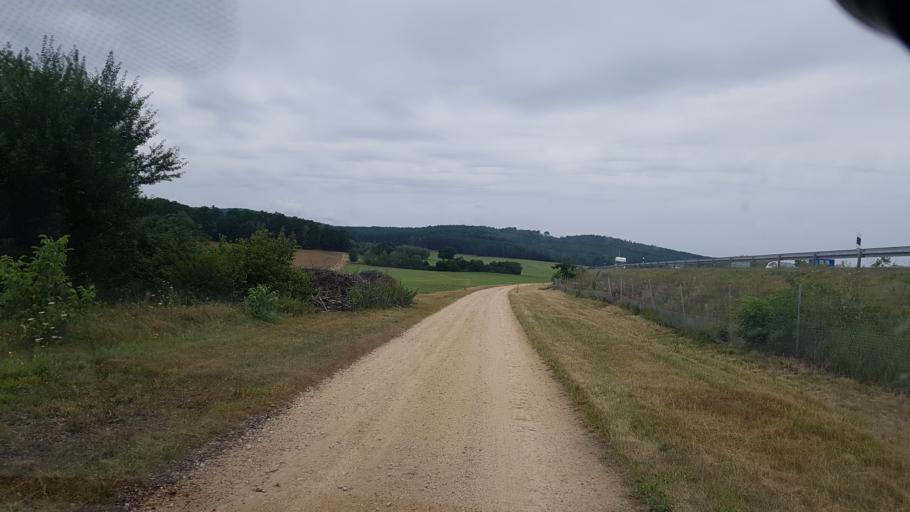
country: DE
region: Saxony
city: Kodersdorf
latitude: 51.2202
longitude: 14.8844
